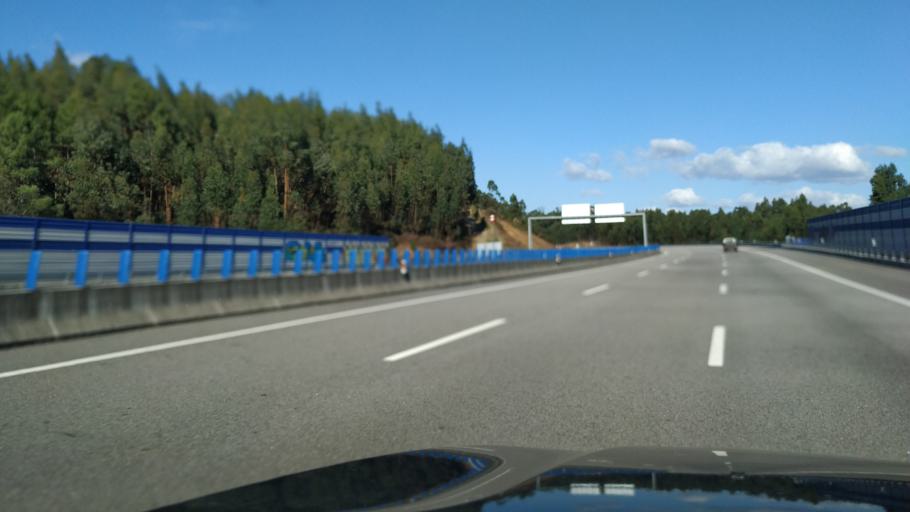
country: PT
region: Porto
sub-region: Vila Nova de Gaia
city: Olival
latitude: 41.0739
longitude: -8.5372
